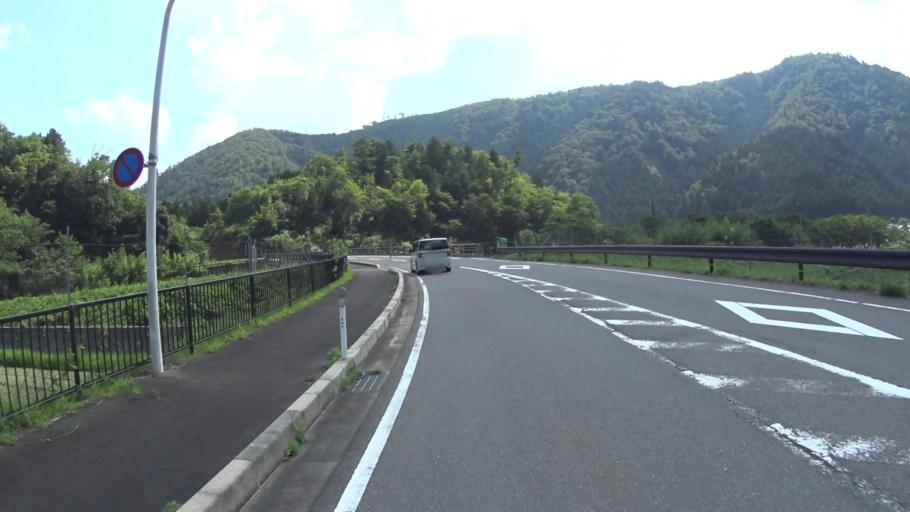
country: JP
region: Kyoto
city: Maizuru
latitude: 35.3123
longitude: 135.5548
